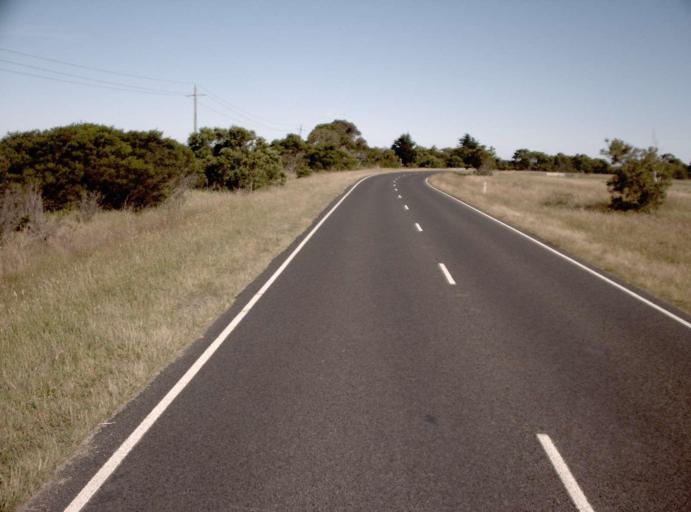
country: AU
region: Victoria
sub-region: Latrobe
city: Traralgon
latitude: -38.6257
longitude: 146.6748
